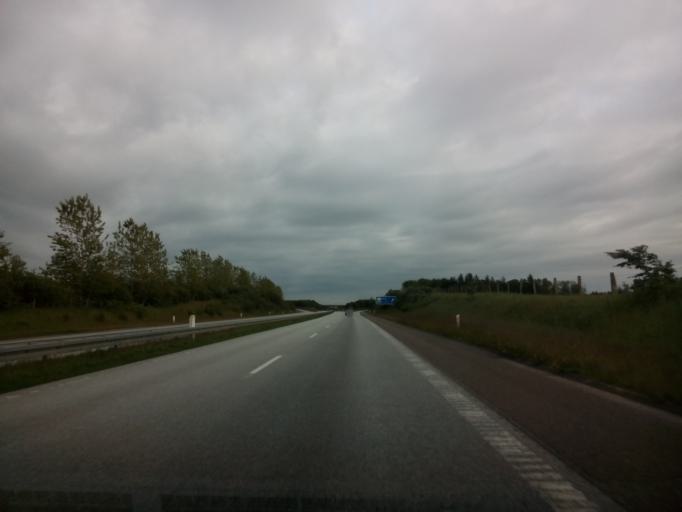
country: DK
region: North Denmark
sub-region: Hjorring Kommune
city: Vra
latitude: 57.3681
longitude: 10.0238
